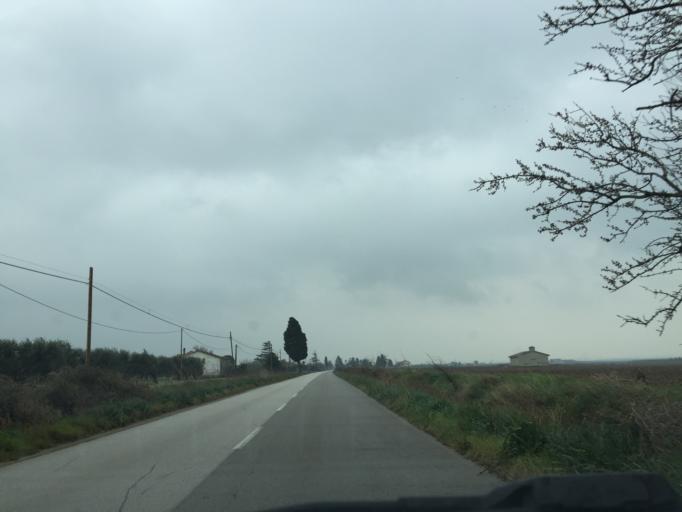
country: IT
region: Apulia
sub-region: Provincia di Foggia
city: Foggia
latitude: 41.4237
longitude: 15.4661
